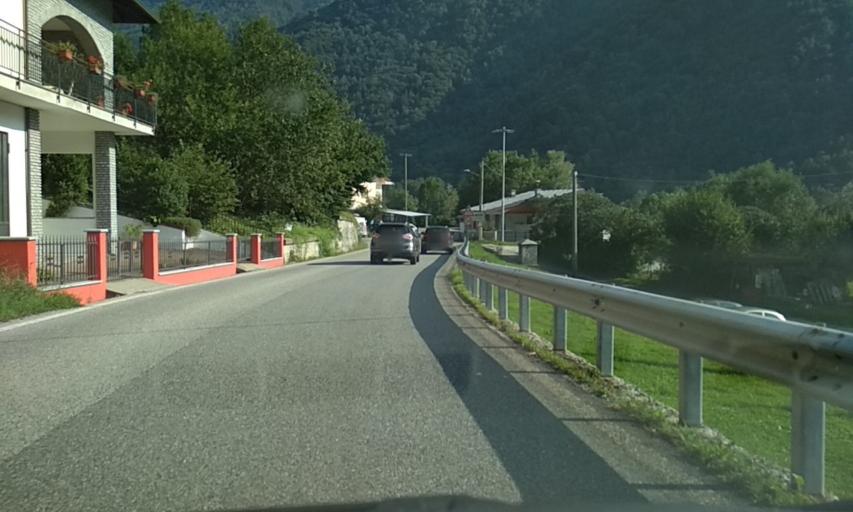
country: IT
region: Piedmont
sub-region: Provincia di Torino
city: Locana
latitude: 45.4107
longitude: 7.4815
